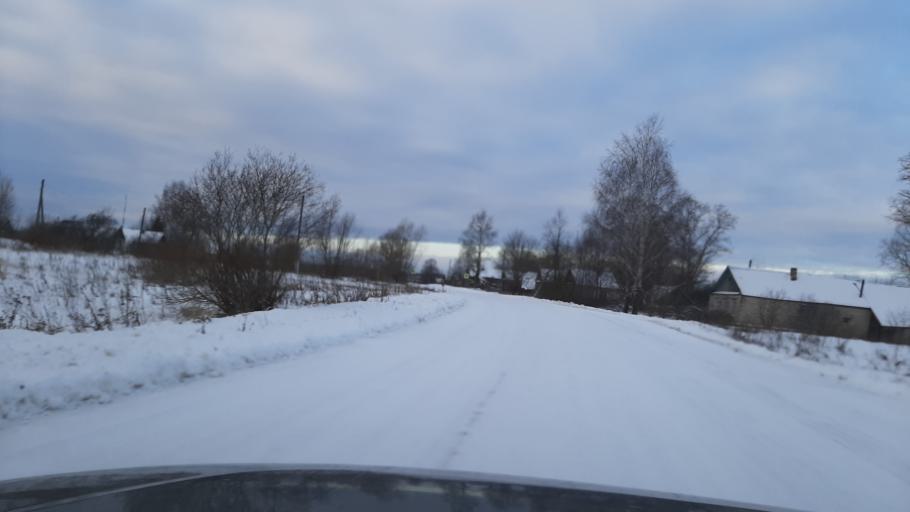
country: RU
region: Kostroma
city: Kosmynino
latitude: 57.4842
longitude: 40.8133
